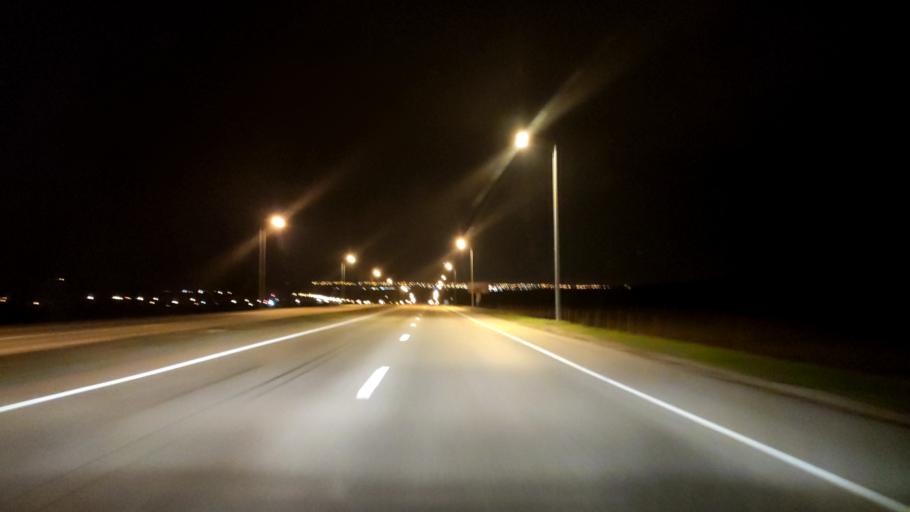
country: RU
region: Belgorod
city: Staryy Oskol
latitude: 51.3388
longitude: 37.7807
